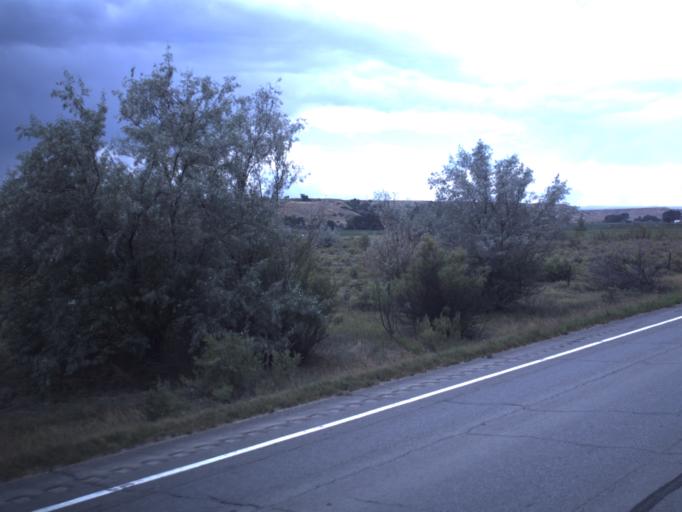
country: US
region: Utah
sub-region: Duchesne County
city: Roosevelt
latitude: 40.1750
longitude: -110.1273
